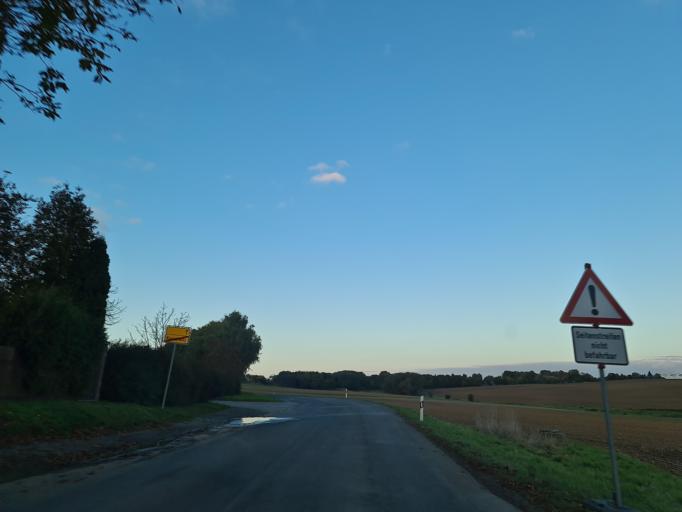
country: DE
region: Saxony
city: Syrau
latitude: 50.5270
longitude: 12.0956
